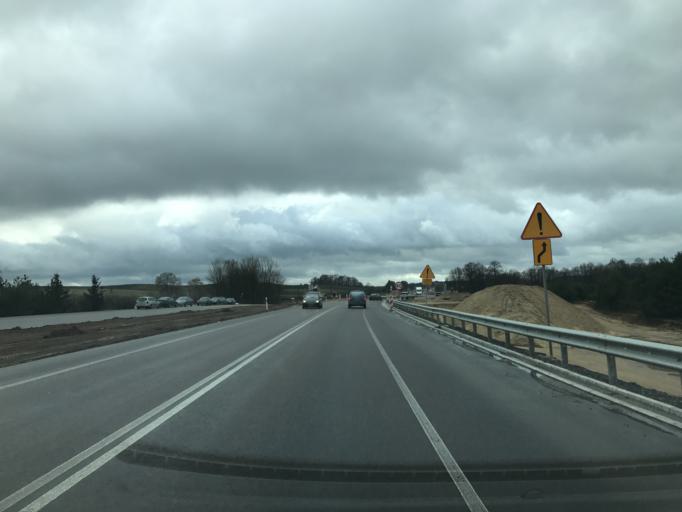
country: PL
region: Warmian-Masurian Voivodeship
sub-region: Powiat olsztynski
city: Olsztynek
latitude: 53.6136
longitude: 20.3309
